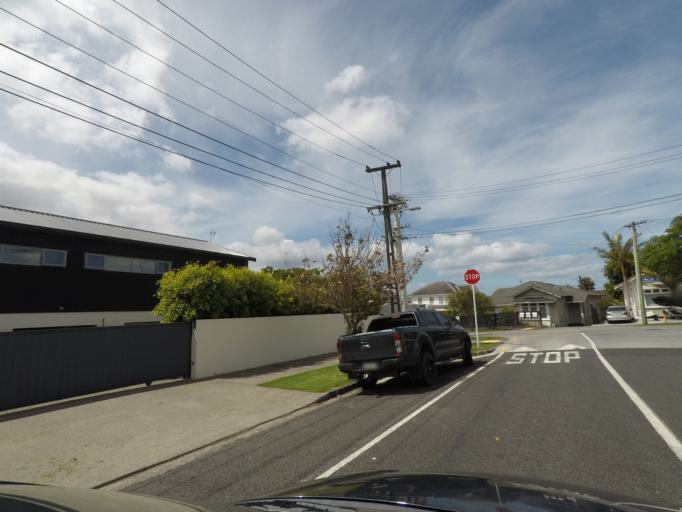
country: NZ
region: Auckland
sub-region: Auckland
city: Auckland
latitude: -36.8429
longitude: 174.7328
